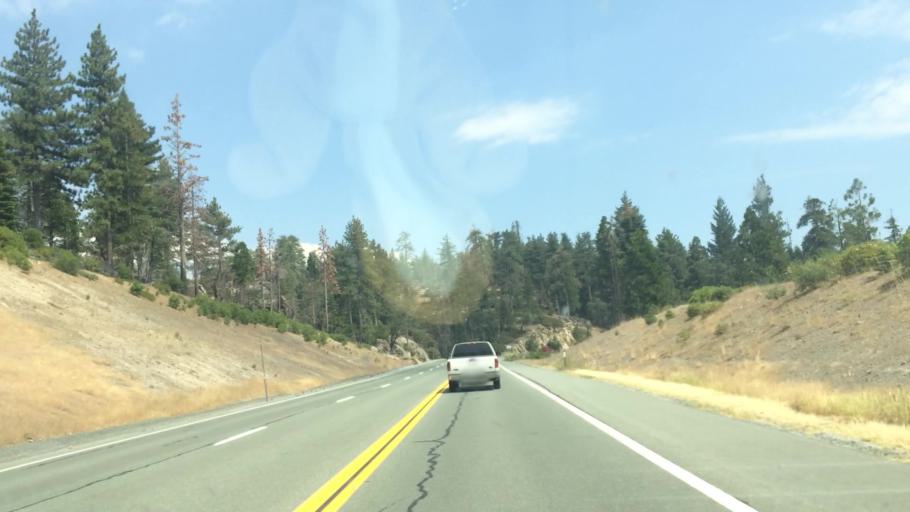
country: US
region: California
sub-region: Amador County
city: Pioneer
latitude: 38.5467
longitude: -120.3542
